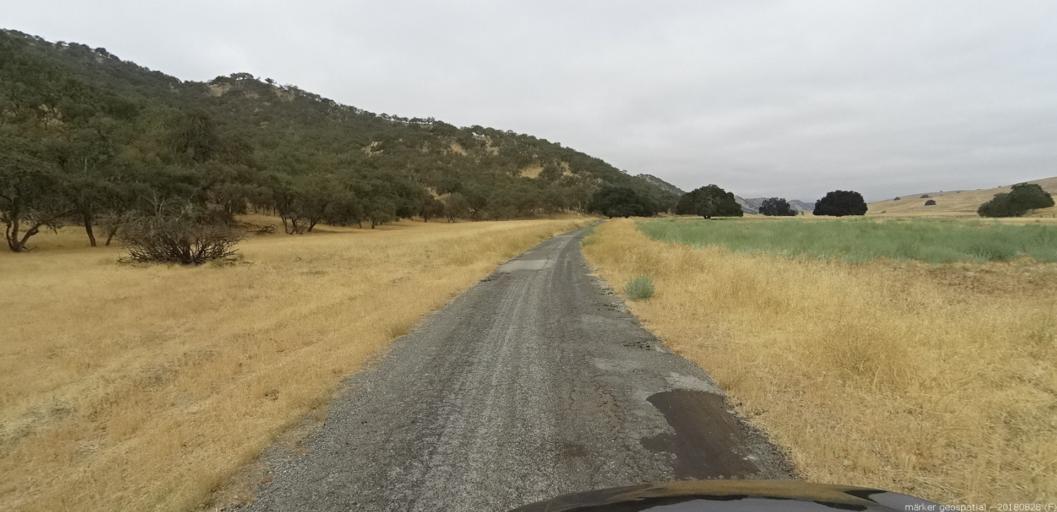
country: US
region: California
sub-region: San Luis Obispo County
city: San Miguel
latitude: 35.9416
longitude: -120.7658
